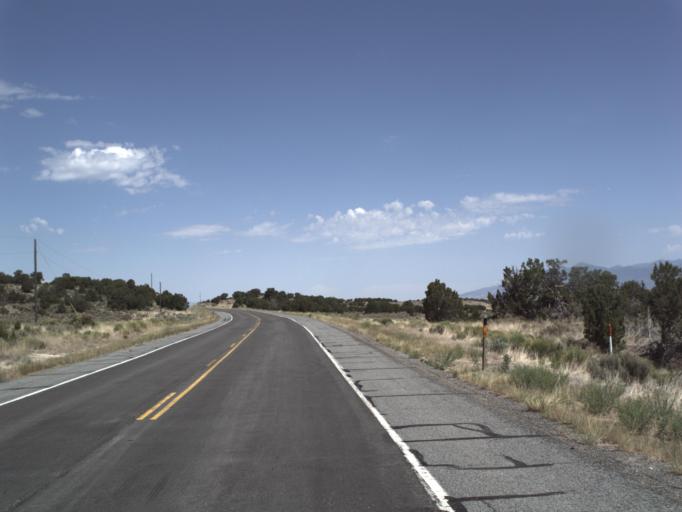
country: US
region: Utah
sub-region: Utah County
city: Eagle Mountain
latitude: 40.0266
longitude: -112.2823
